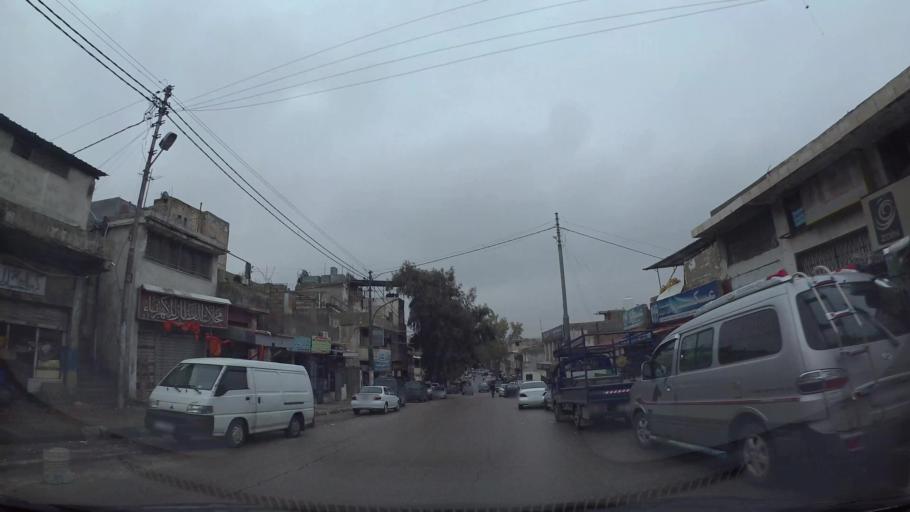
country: JO
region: Amman
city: Amman
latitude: 31.9617
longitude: 35.9278
